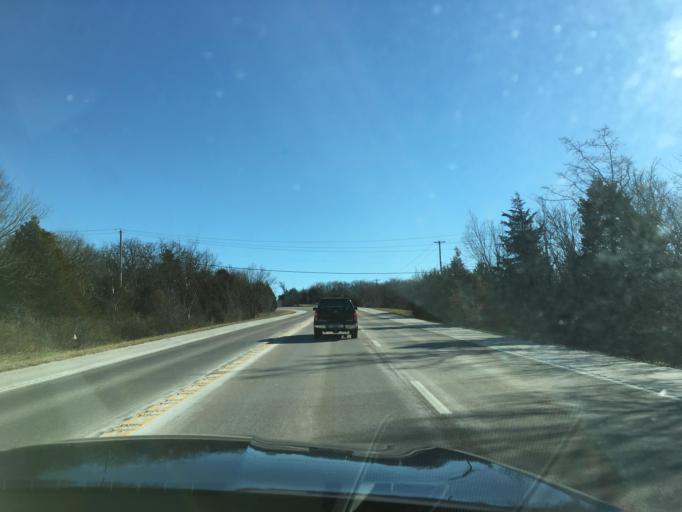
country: US
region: Missouri
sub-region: Jefferson County
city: De Soto
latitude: 38.1361
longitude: -90.4789
